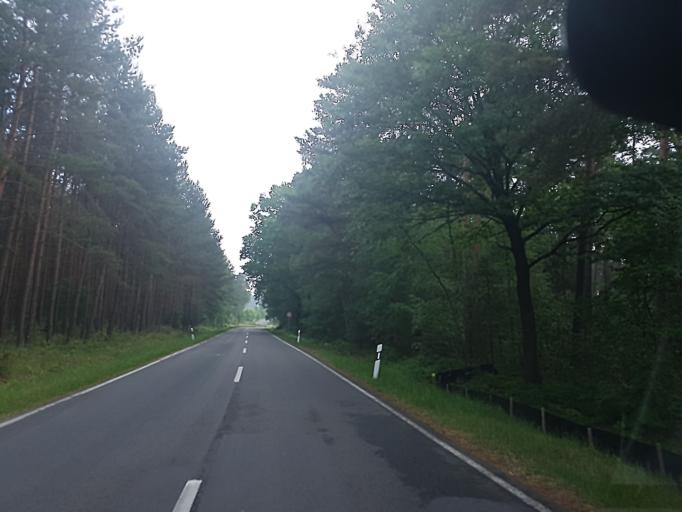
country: DE
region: Brandenburg
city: Gorzke
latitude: 52.0899
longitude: 12.3332
